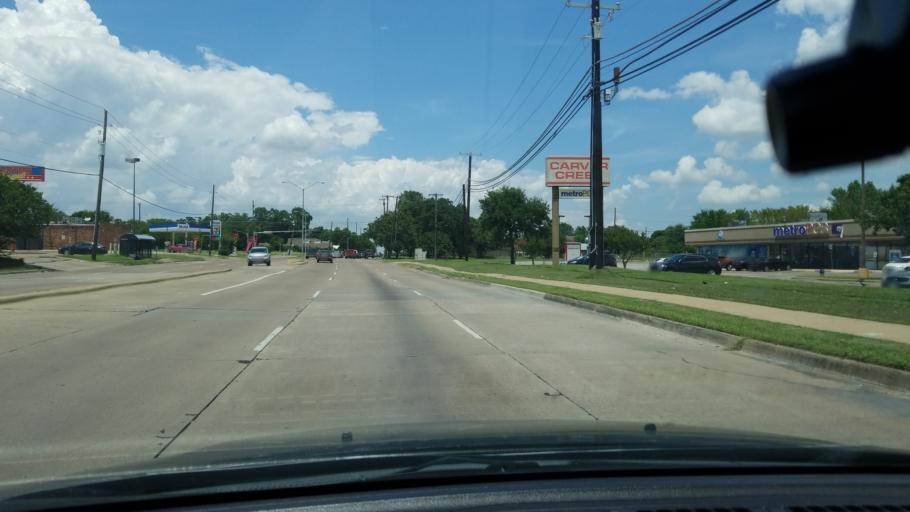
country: US
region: Texas
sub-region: Dallas County
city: Balch Springs
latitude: 32.7470
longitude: -96.6482
